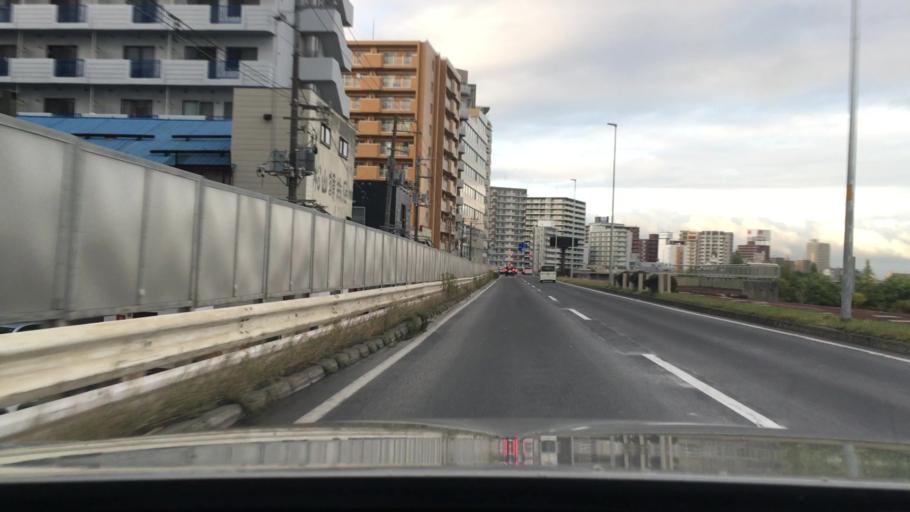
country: JP
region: Hokkaido
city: Sapporo
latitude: 43.0504
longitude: 141.3592
